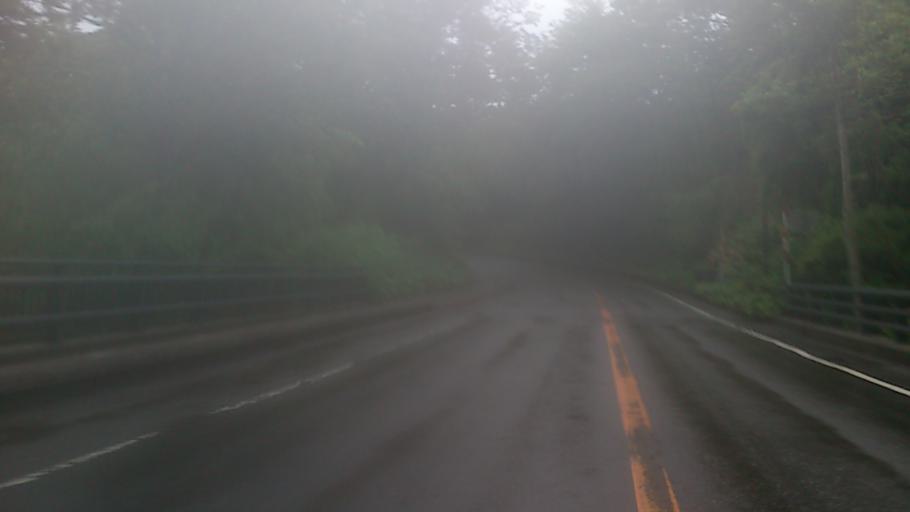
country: JP
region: Hokkaido
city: Shiraoi
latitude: 42.7688
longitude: 141.4152
